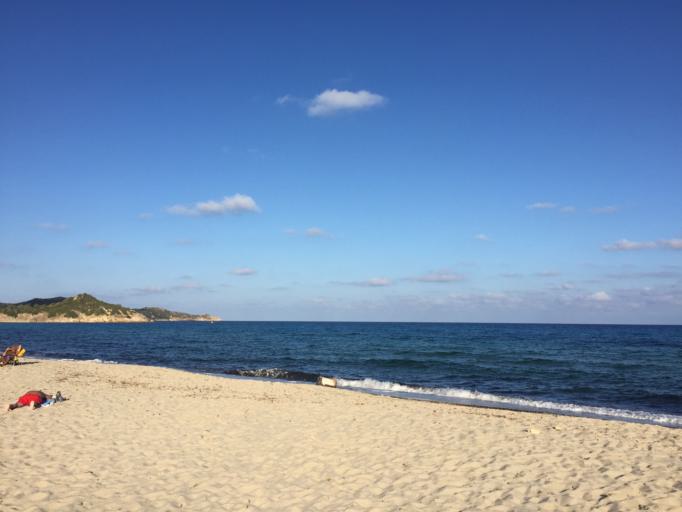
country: IT
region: Sardinia
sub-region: Provincia di Cagliari
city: Olia Speciosa
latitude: 39.2918
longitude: 9.6034
